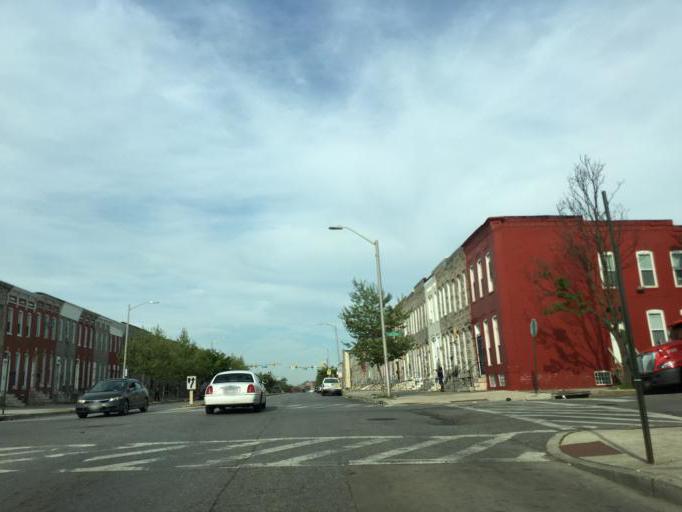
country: US
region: Maryland
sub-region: Baltimore County
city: Lansdowne
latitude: 39.2806
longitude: -76.6508
